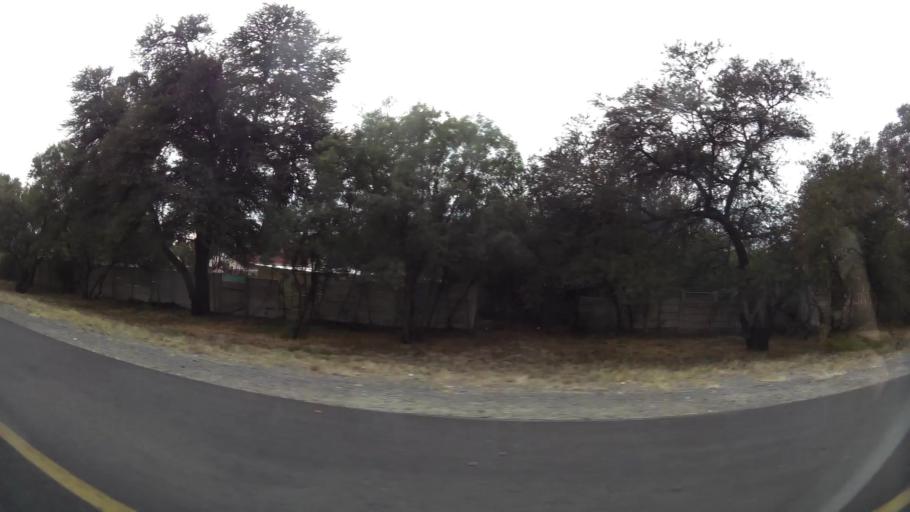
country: ZA
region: Orange Free State
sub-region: Mangaung Metropolitan Municipality
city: Bloemfontein
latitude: -29.1439
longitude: 26.1707
